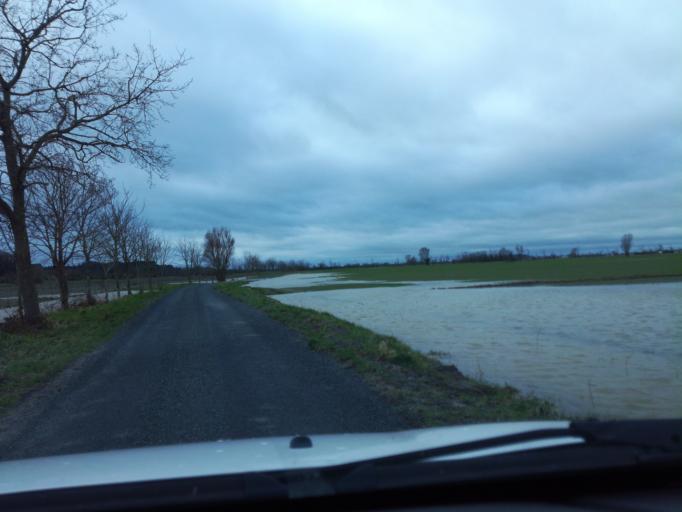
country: FR
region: Brittany
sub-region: Departement d'Ille-et-Vilaine
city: Saint-Broladre
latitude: 48.5859
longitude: -1.6792
